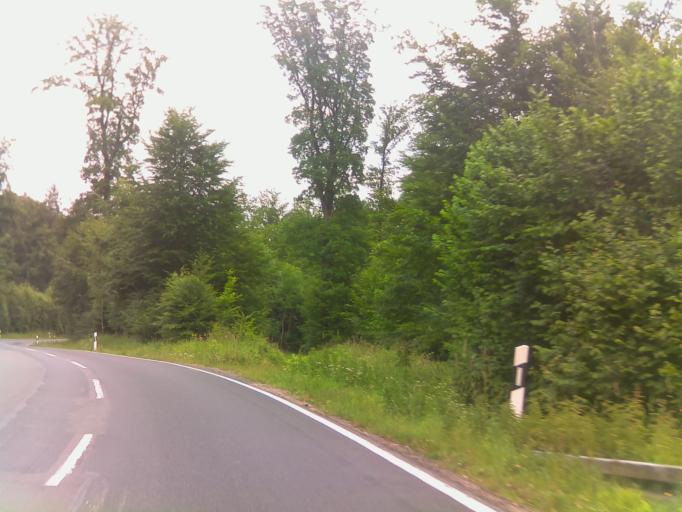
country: DE
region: Lower Saxony
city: Vahlbruch
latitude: 51.8913
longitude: 9.3245
